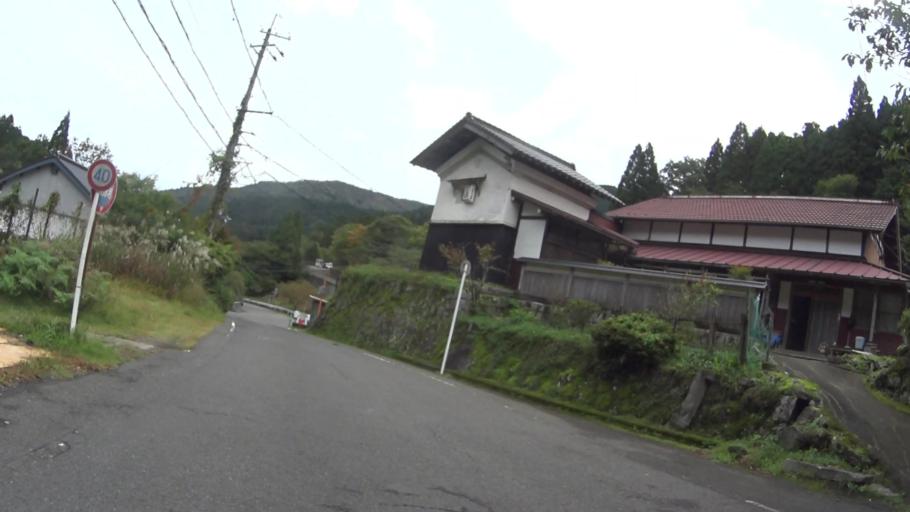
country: JP
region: Shiga Prefecture
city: Kitahama
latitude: 35.1719
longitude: 135.7828
